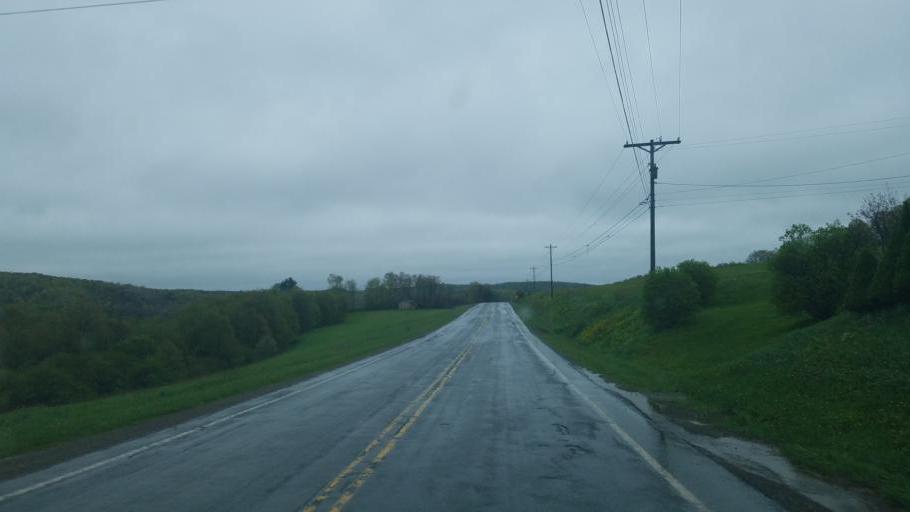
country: US
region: Pennsylvania
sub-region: Potter County
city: Coudersport
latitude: 41.8393
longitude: -77.8920
